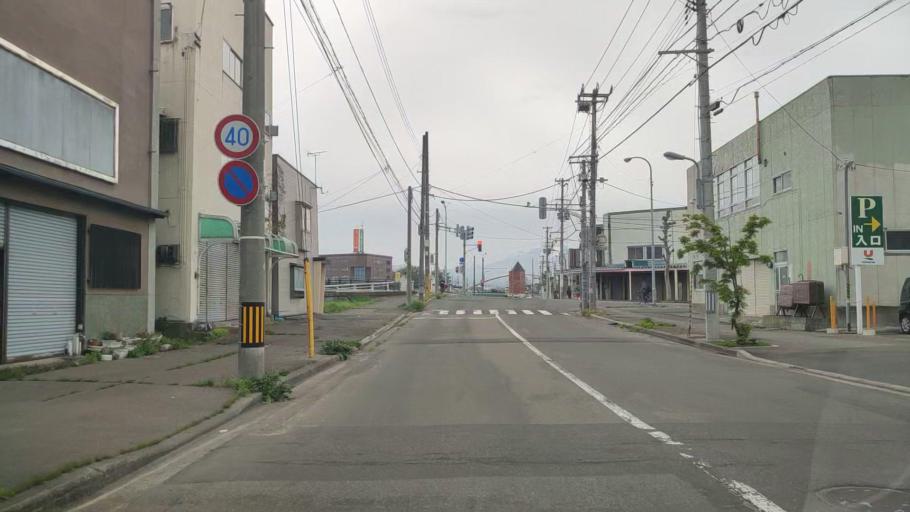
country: JP
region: Aomori
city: Aomori Shi
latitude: 40.8261
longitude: 140.7600
